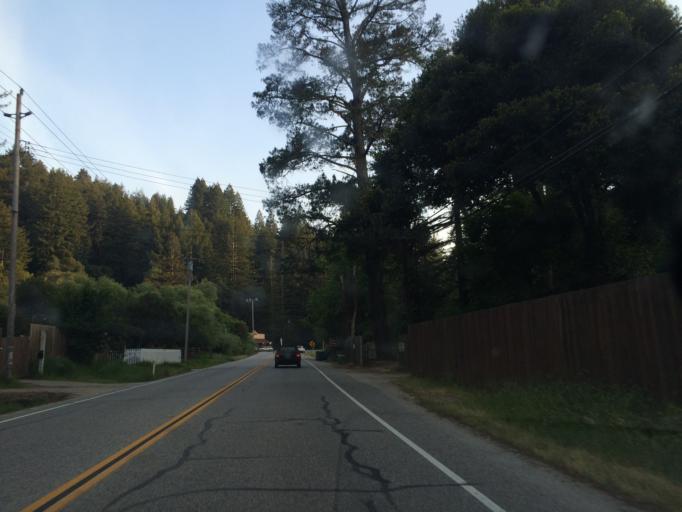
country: US
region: California
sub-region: Santa Cruz County
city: Boulder Creek
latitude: 37.1548
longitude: -122.1335
